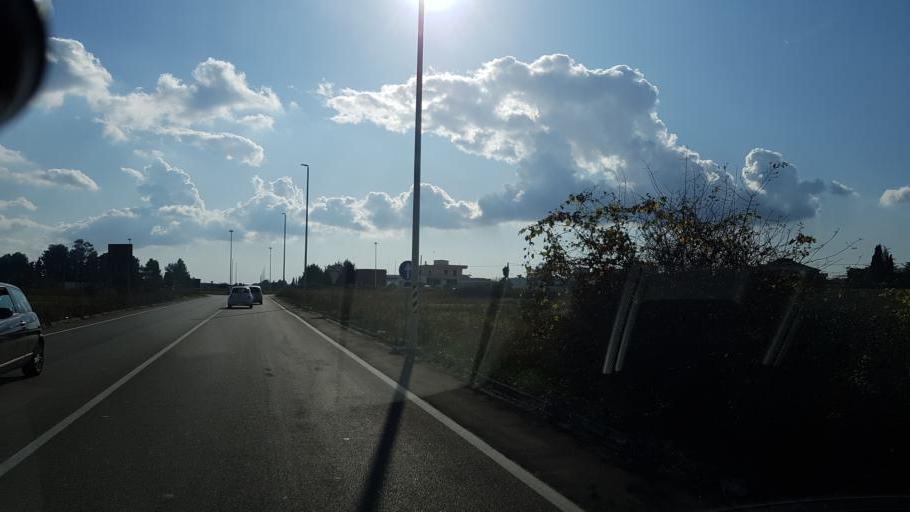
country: IT
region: Apulia
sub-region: Provincia di Lecce
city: Salice Salentino
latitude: 40.3823
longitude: 17.9702
